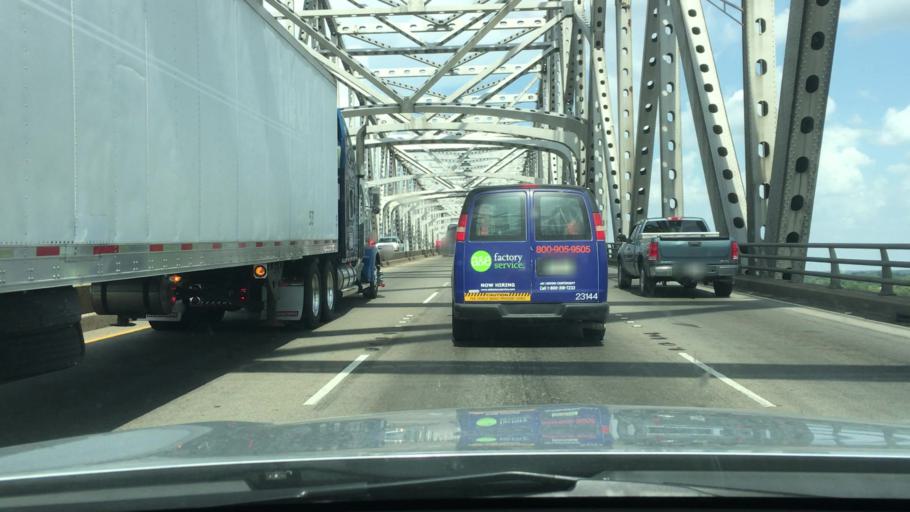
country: US
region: Louisiana
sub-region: West Baton Rouge Parish
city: Port Allen
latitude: 30.4397
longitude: -91.2016
